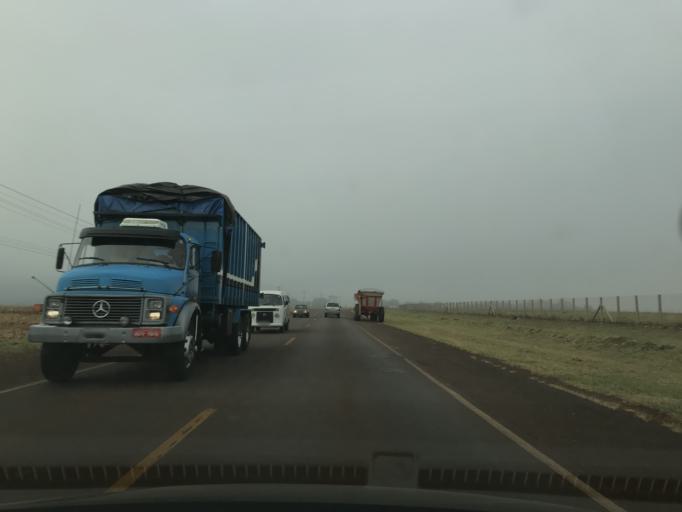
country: BR
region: Parana
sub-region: Toledo
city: Toledo
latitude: -24.6922
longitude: -53.6962
